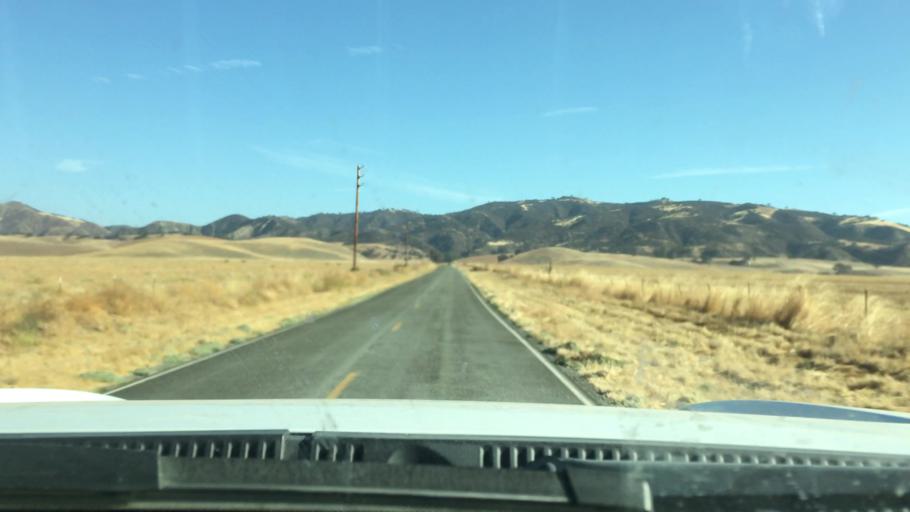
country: US
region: California
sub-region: Monterey County
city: King City
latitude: 36.3894
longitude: -121.0033
